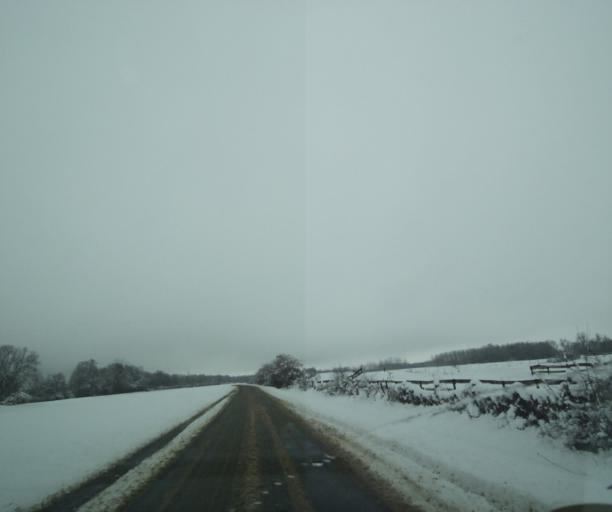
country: FR
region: Champagne-Ardenne
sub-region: Departement de la Haute-Marne
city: Wassy
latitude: 48.5663
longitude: 4.8934
